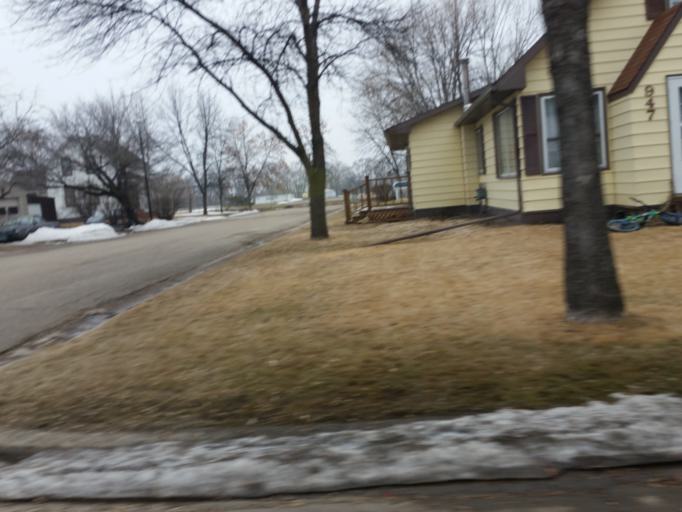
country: US
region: North Dakota
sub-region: Walsh County
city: Grafton
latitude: 48.4146
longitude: -97.4202
